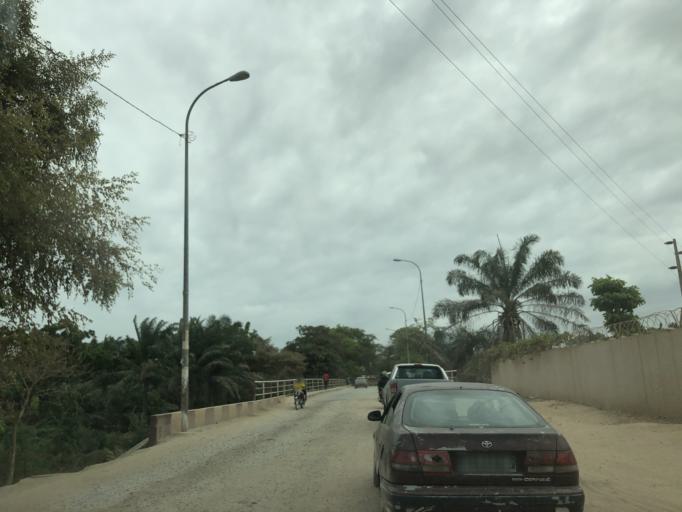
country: AO
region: Cuanza Sul
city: Sumbe
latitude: -11.1990
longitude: 13.8464
